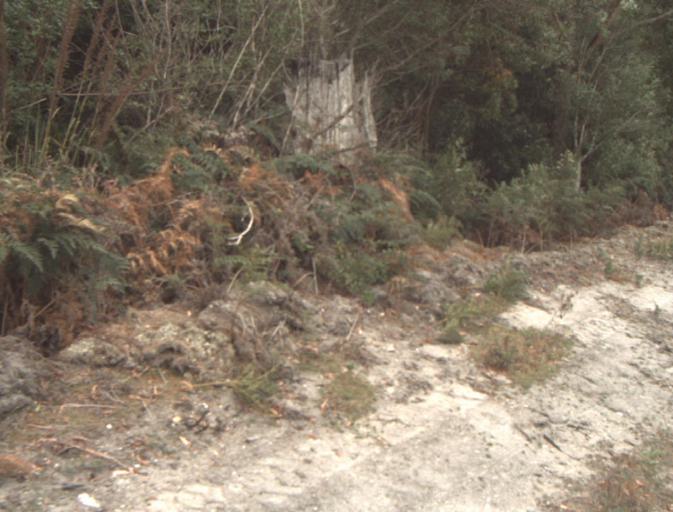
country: AU
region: Tasmania
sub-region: Launceston
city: Mayfield
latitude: -41.1642
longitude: 147.1785
